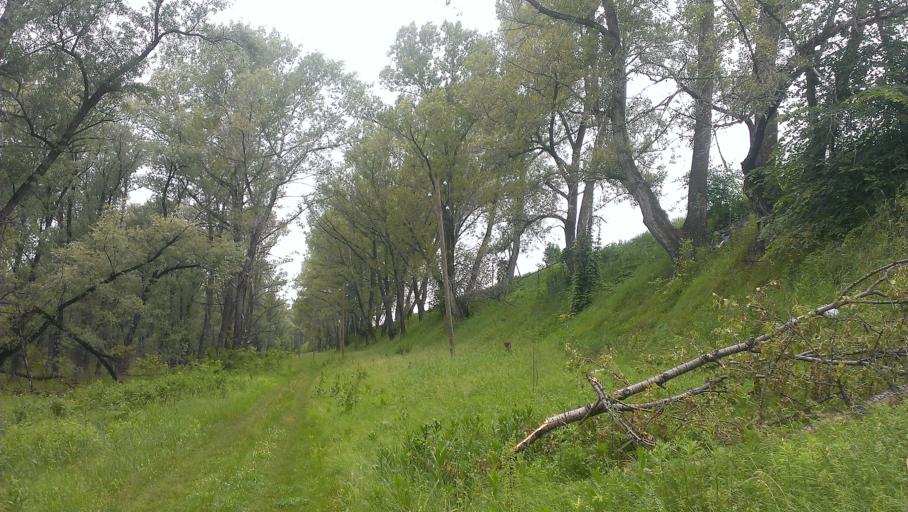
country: RU
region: Altai Krai
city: Beloyarsk
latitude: 53.4543
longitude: 83.8710
